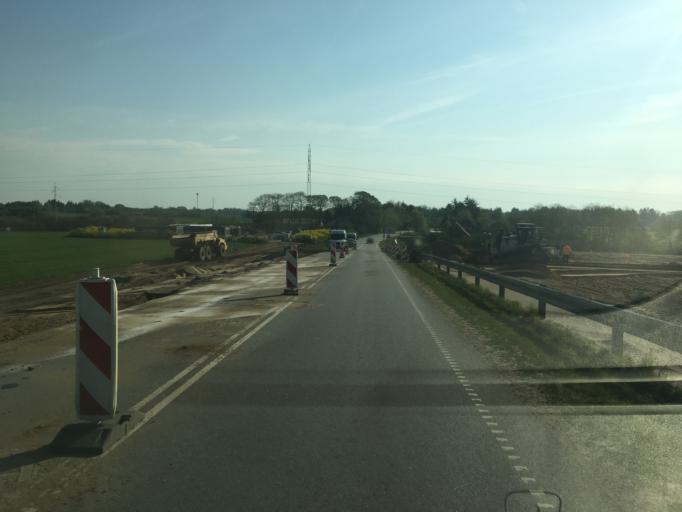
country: DK
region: South Denmark
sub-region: Aabenraa Kommune
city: Aabenraa
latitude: 55.0810
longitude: 9.3750
